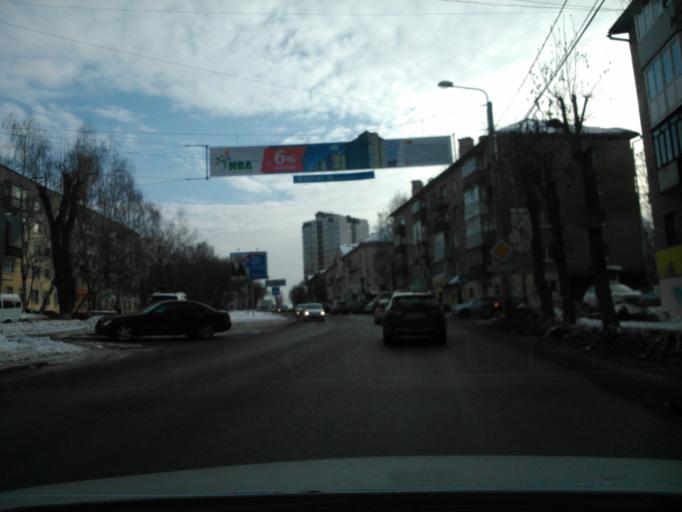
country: RU
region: Perm
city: Perm
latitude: 58.0019
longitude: 56.2389
